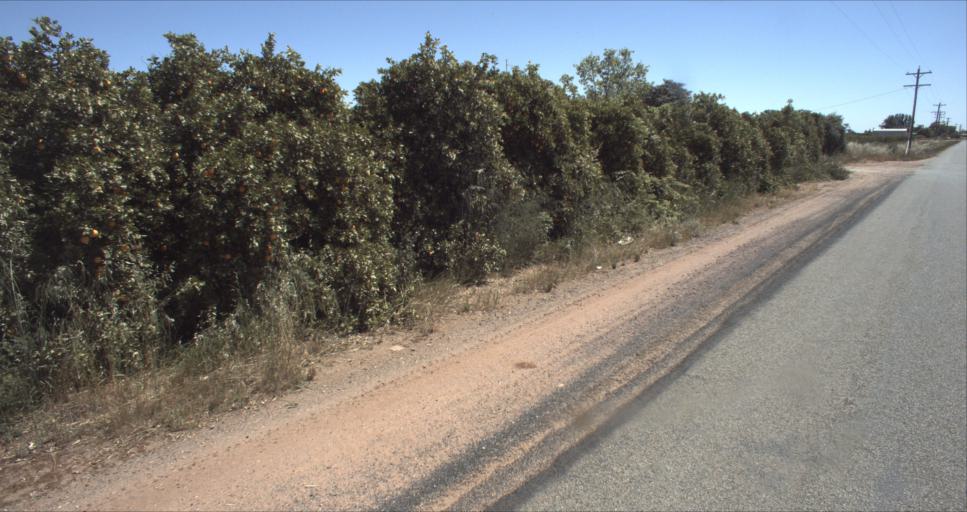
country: AU
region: New South Wales
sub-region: Leeton
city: Leeton
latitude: -34.5404
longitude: 146.3624
